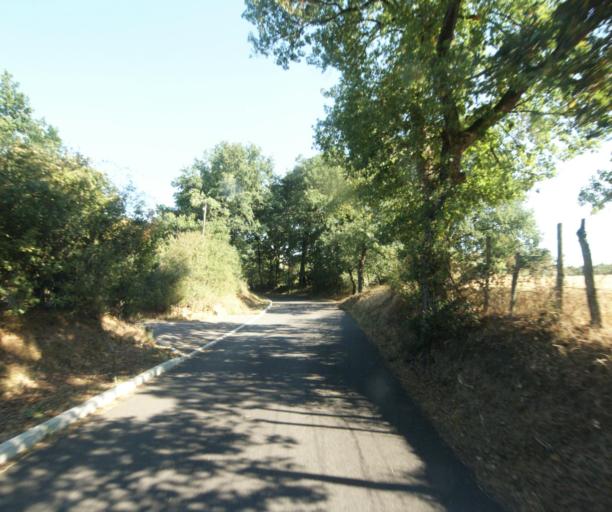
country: FR
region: Rhone-Alpes
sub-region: Departement du Rhone
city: Sainte-Consorce
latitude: 45.8012
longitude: 4.6916
